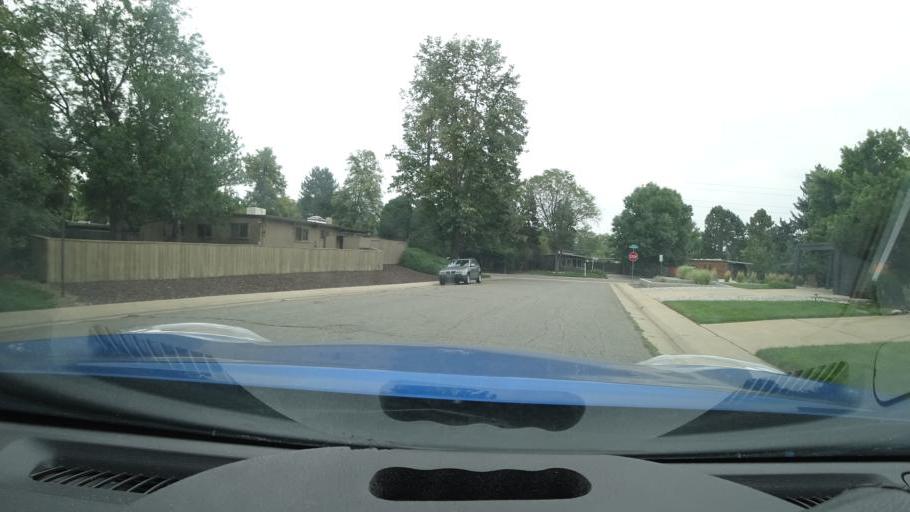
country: US
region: Colorado
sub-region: Arapahoe County
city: Glendale
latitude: 39.6834
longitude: -104.9189
